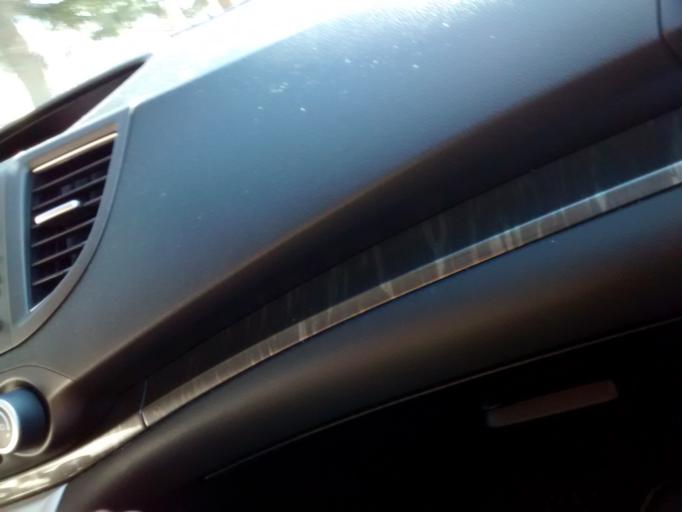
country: US
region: Massachusetts
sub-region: Worcester County
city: Uxbridge
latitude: 42.0946
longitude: -71.6382
